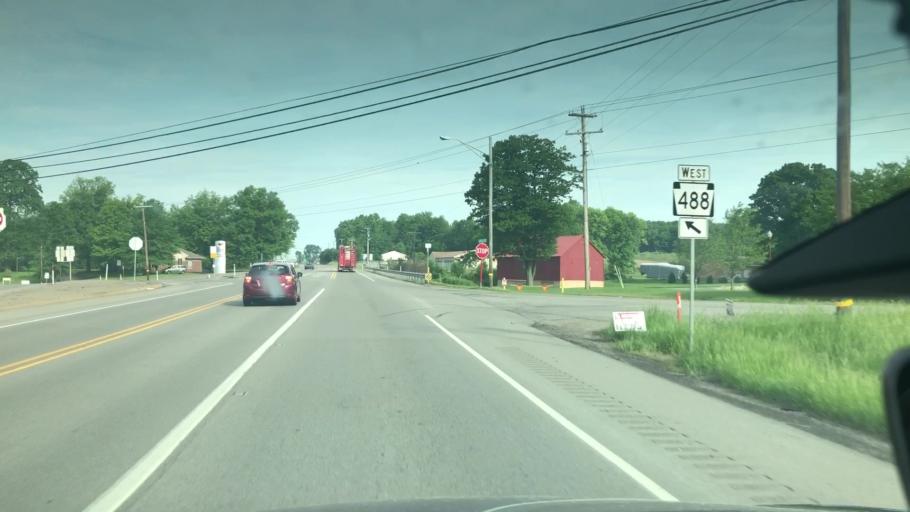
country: US
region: Pennsylvania
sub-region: Butler County
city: Prospect
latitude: 40.9054
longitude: -80.0213
